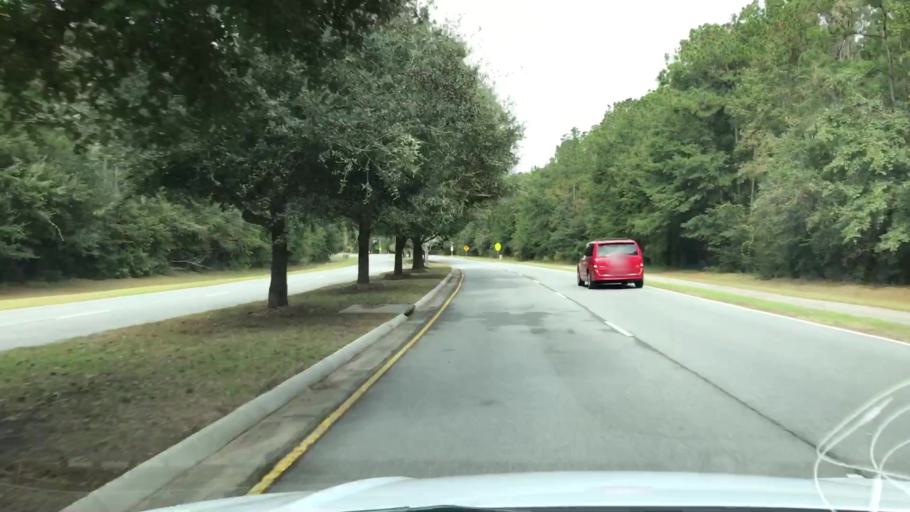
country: US
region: South Carolina
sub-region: Beaufort County
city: Bluffton
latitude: 32.2418
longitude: -80.9020
